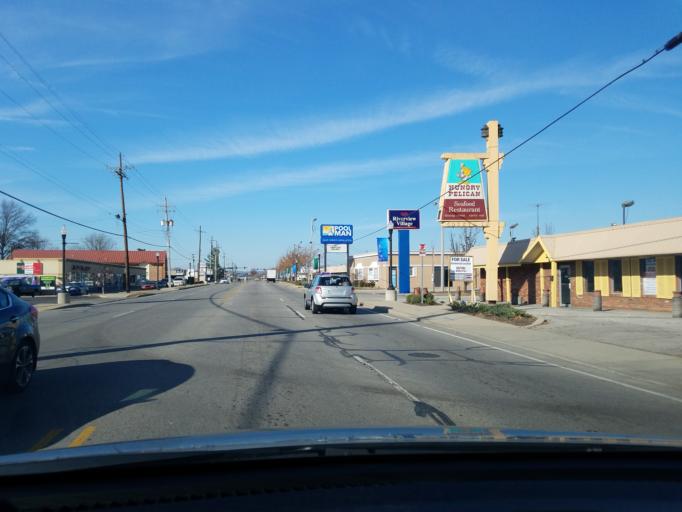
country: US
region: Indiana
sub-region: Clark County
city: Clarksville
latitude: 38.2983
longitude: -85.7610
